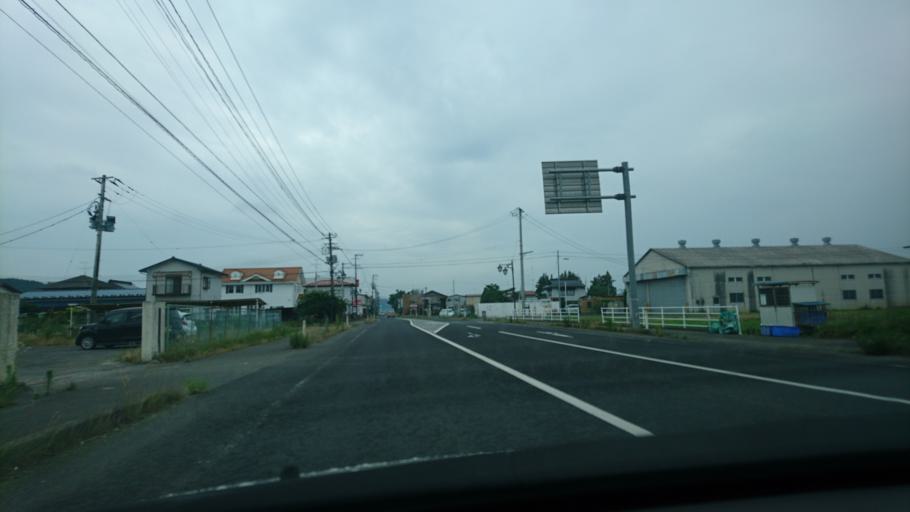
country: JP
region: Miyagi
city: Furukawa
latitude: 38.7342
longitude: 140.9583
